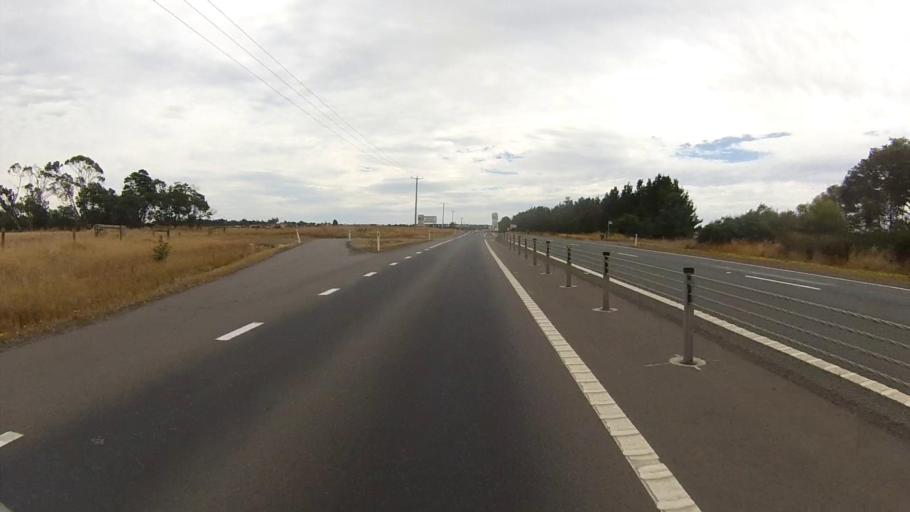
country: AU
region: Tasmania
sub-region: Northern Midlands
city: Evandale
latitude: -41.6405
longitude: 147.2336
